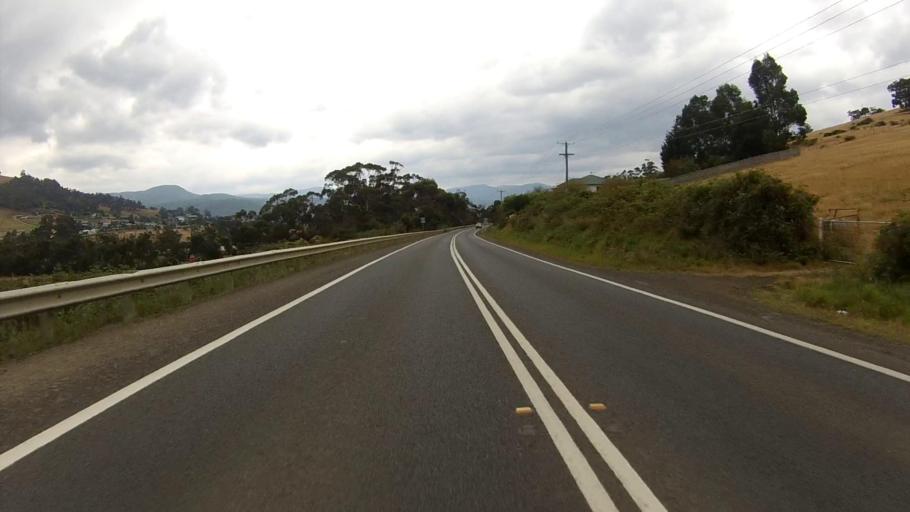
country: AU
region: Tasmania
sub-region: Huon Valley
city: Huonville
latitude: -43.0471
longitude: 147.0507
